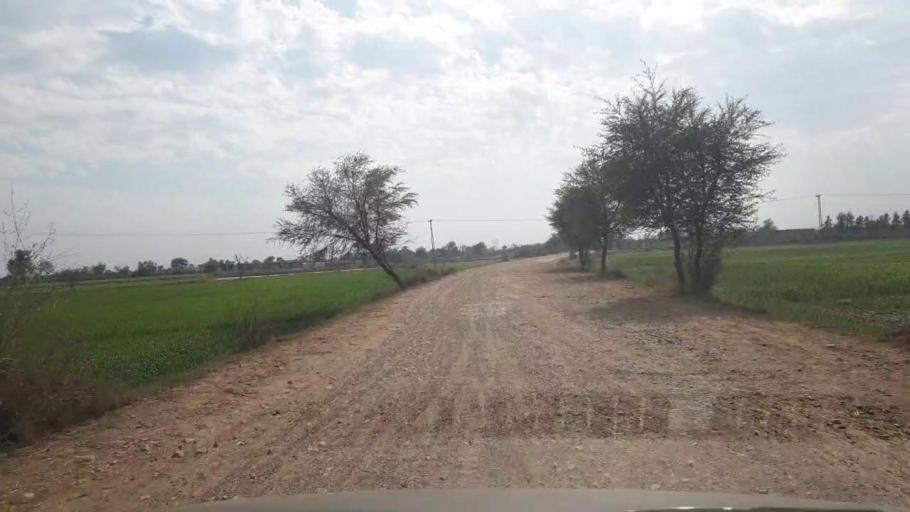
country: PK
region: Sindh
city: Sakrand
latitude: 26.0061
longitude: 68.4054
